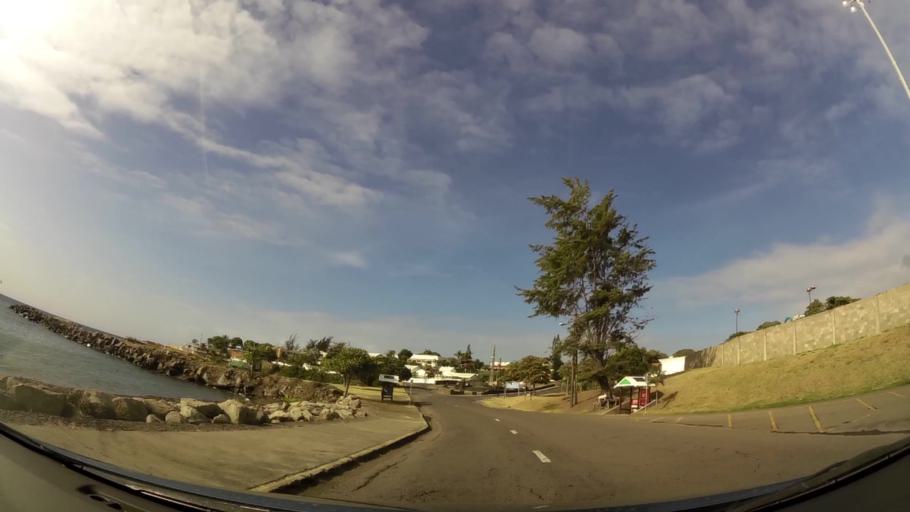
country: KN
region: Saint George Basseterre
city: Basseterre
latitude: 17.2928
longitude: -62.7312
